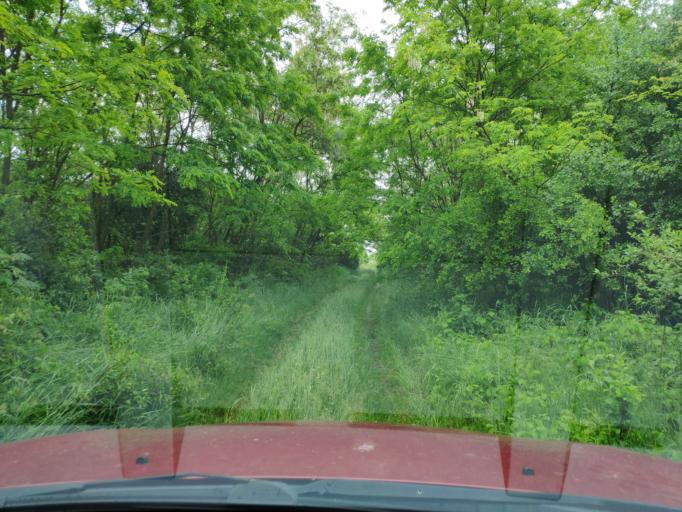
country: SK
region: Kosicky
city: Cierna nad Tisou
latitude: 48.4260
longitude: 22.0755
